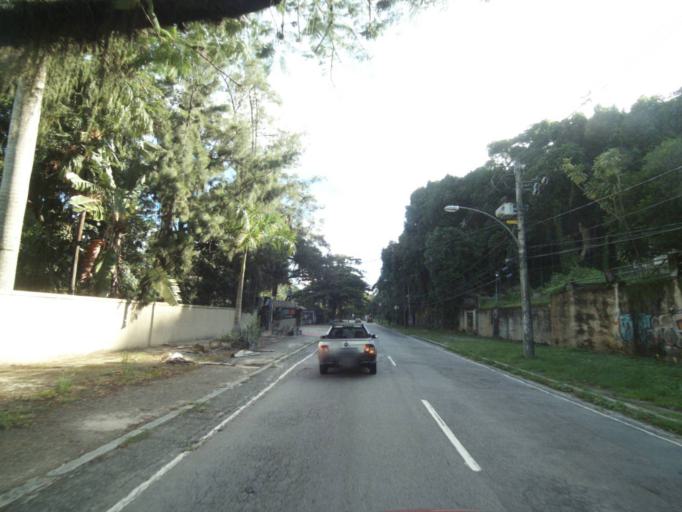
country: BR
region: Rio de Janeiro
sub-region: Rio De Janeiro
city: Rio de Janeiro
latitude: -22.9277
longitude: -43.3205
